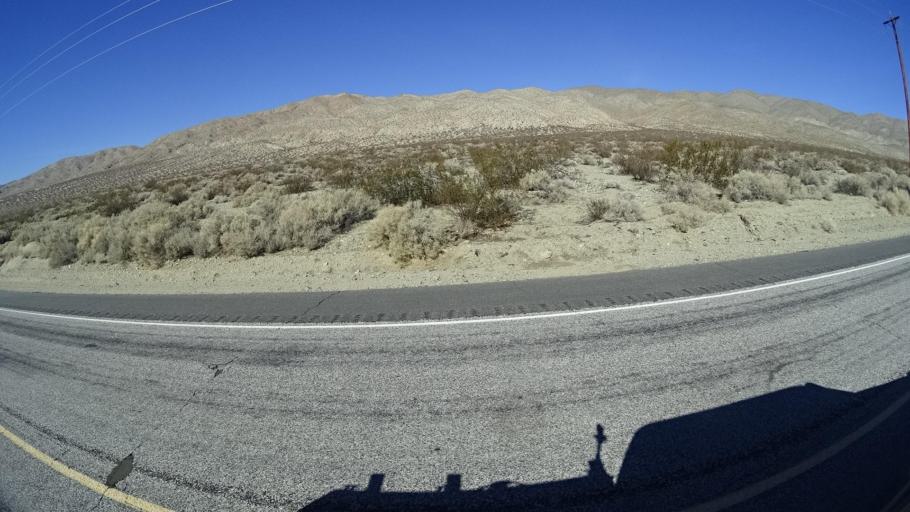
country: US
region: California
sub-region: Kern County
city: California City
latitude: 35.3717
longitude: -117.8772
